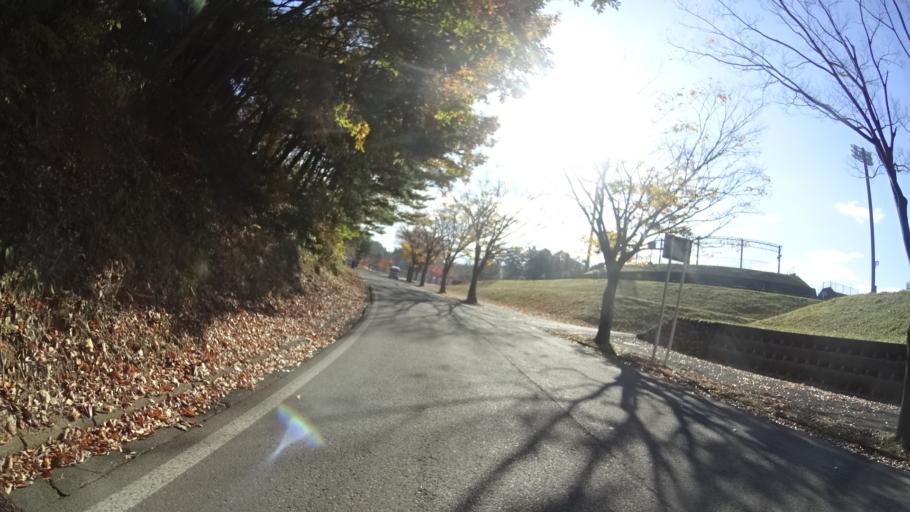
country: JP
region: Niigata
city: Itoigawa
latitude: 37.0245
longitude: 137.8652
